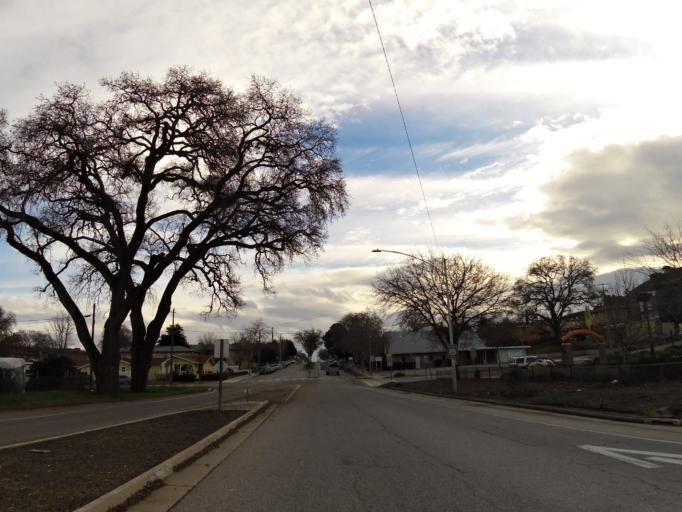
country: US
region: California
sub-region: San Luis Obispo County
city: Paso Robles
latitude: 35.6522
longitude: -120.6936
